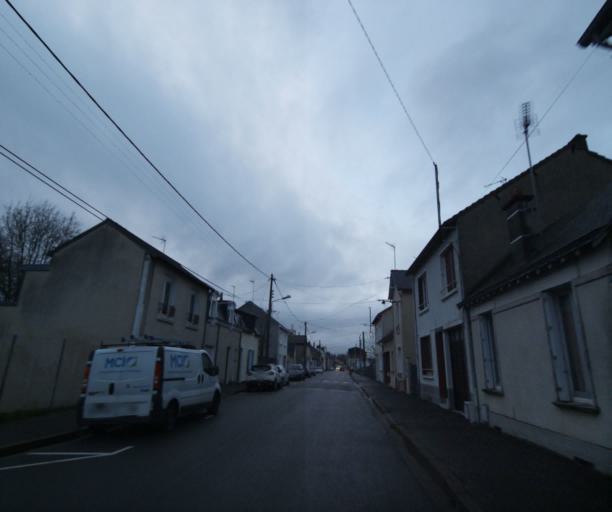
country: FR
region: Pays de la Loire
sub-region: Departement de la Sarthe
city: Coulaines
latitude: 48.0159
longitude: 0.1964
